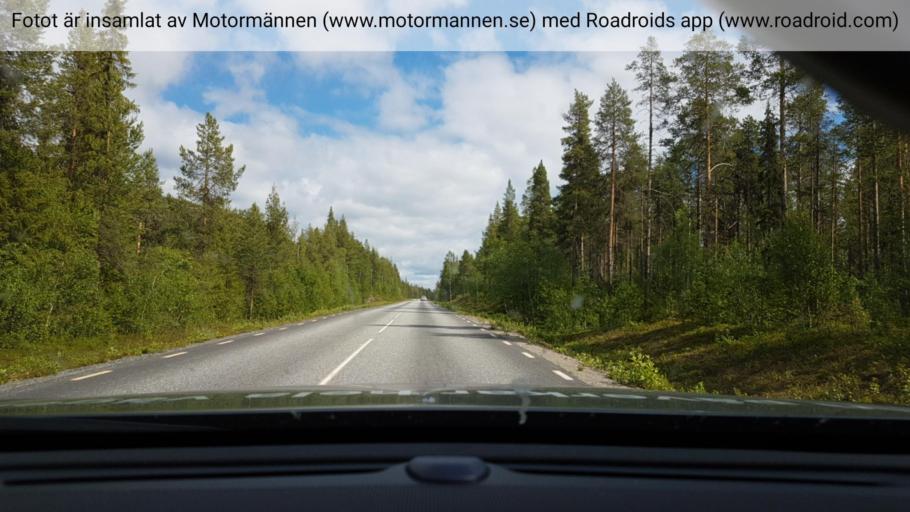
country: SE
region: Vaesterbotten
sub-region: Sorsele Kommun
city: Sorsele
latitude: 65.6916
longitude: 17.1852
